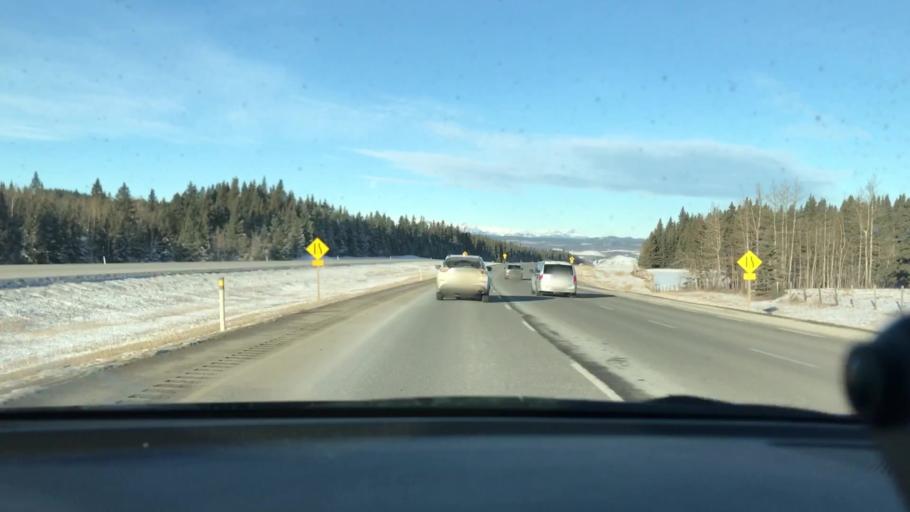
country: CA
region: Alberta
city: Cochrane
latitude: 51.1471
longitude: -114.7340
